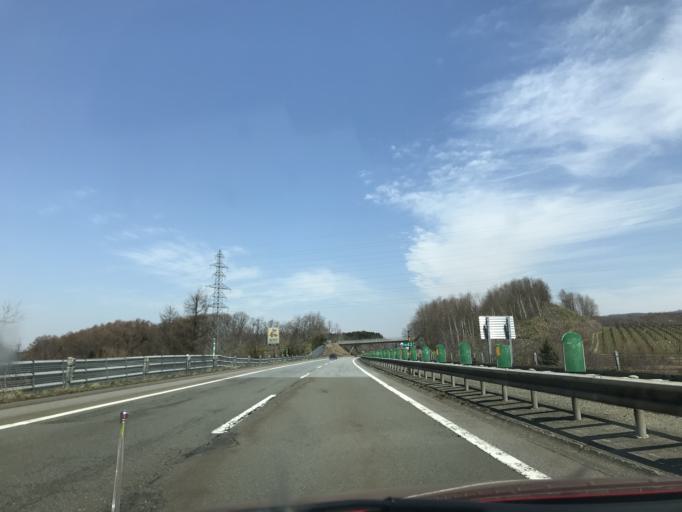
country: JP
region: Hokkaido
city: Bibai
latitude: 43.2543
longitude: 141.8322
